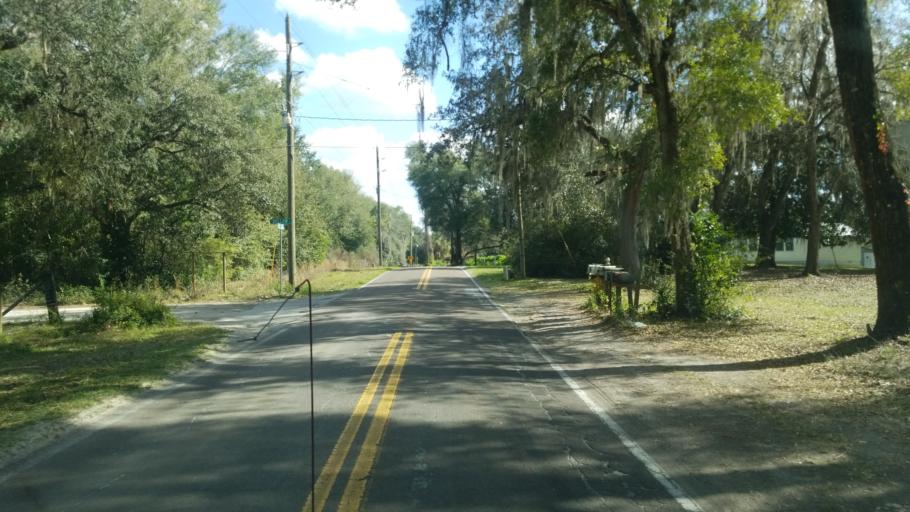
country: US
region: Florida
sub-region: Citrus County
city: Floral City
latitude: 28.7513
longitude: -82.2550
